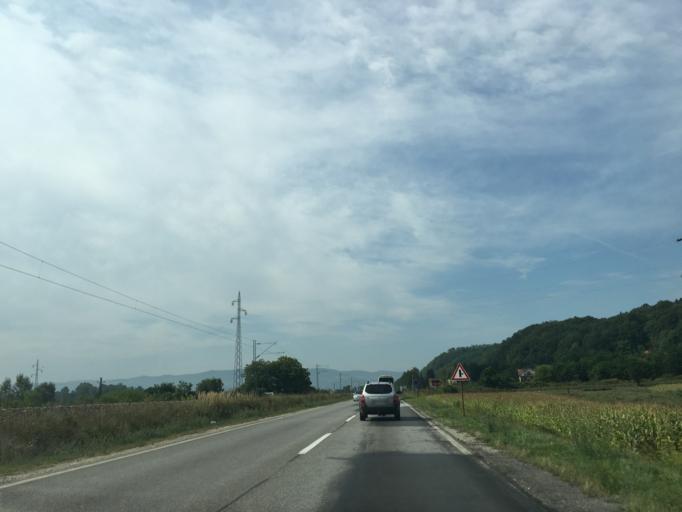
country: RS
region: Central Serbia
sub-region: Zlatiborski Okrug
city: Pozega
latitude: 43.8596
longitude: 20.0843
